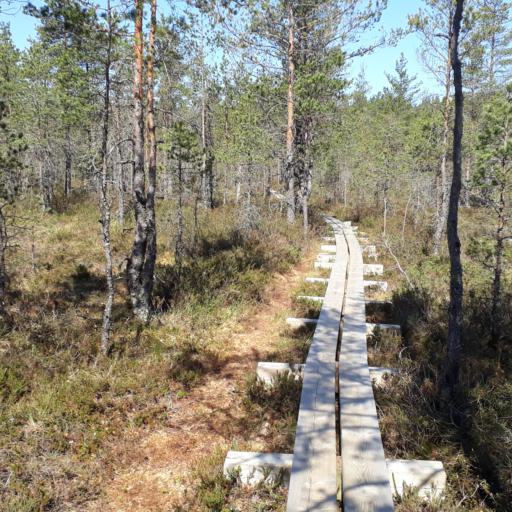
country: EE
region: Harju
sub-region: Loksa linn
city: Loksa
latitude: 59.4787
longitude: 25.6643
